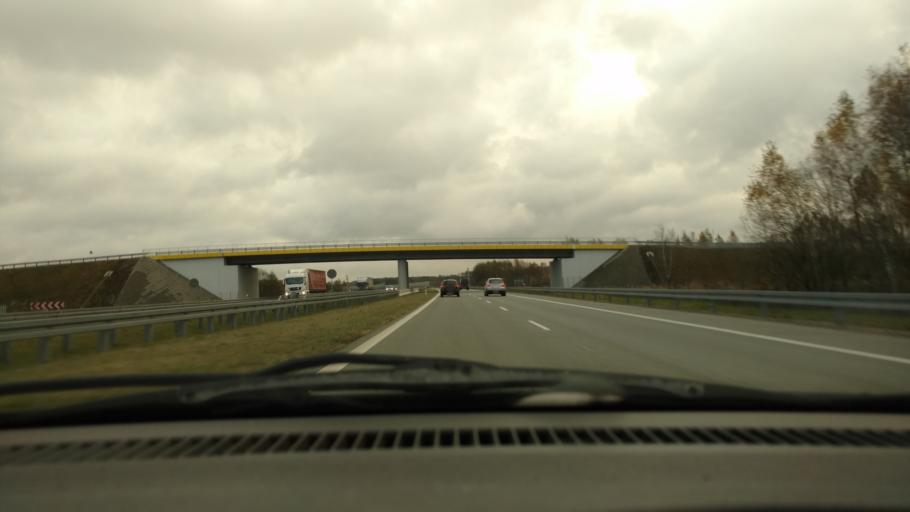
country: PL
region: Lodz Voivodeship
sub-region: Powiat lodzki wschodni
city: Rzgow
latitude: 51.6329
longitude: 19.4518
